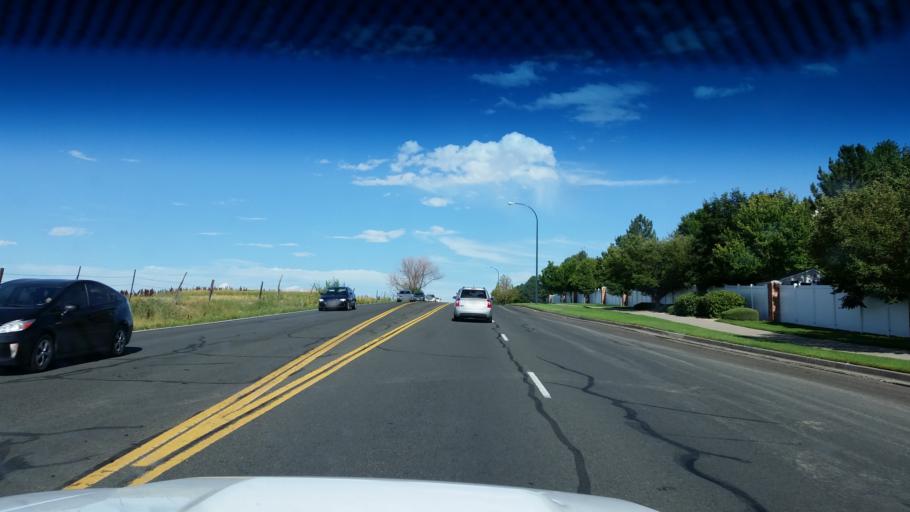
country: US
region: Colorado
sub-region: Adams County
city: Northglenn
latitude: 39.9285
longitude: -105.0036
